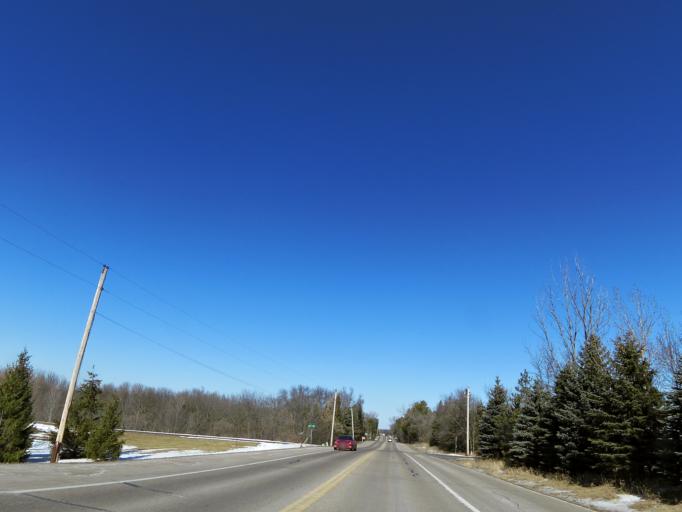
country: US
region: Minnesota
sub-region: Washington County
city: Lake Elmo
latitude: 45.0439
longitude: -92.8835
